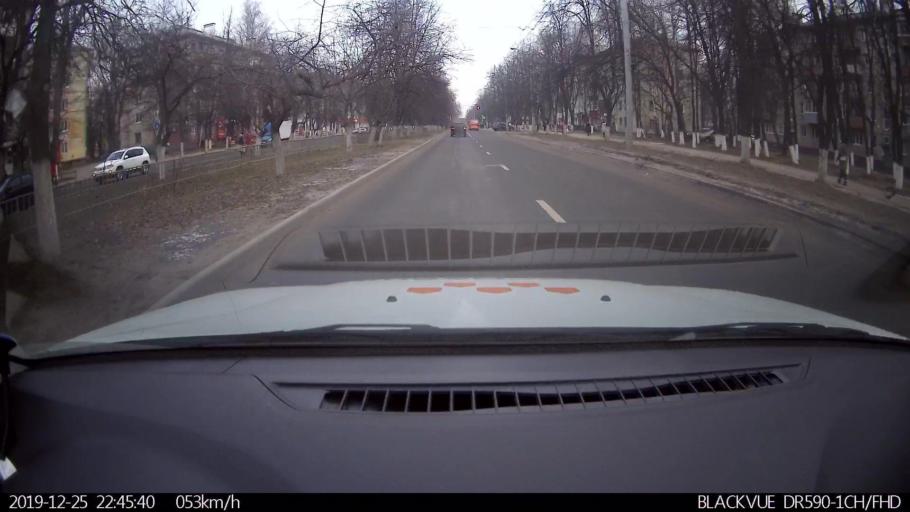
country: RU
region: Nizjnij Novgorod
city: Burevestnik
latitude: 56.2346
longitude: 43.8602
